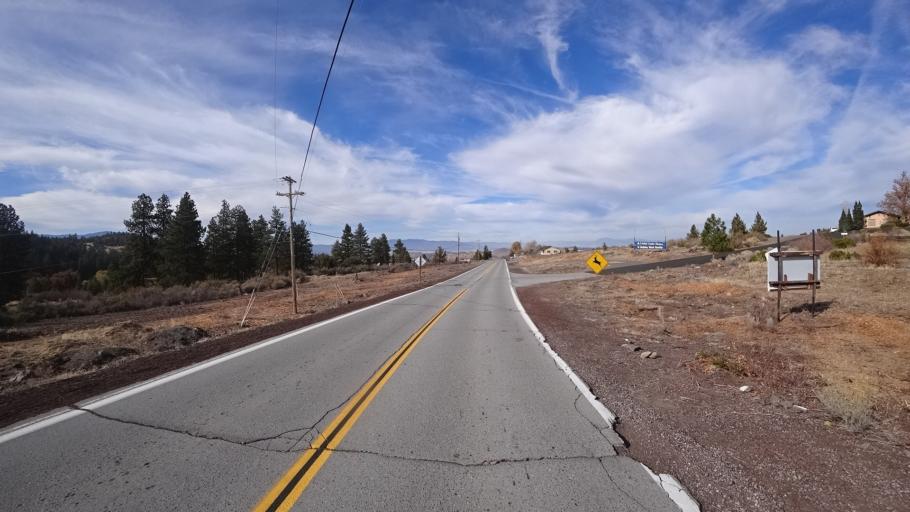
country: US
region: California
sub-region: Siskiyou County
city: Weed
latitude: 41.4731
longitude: -122.3526
